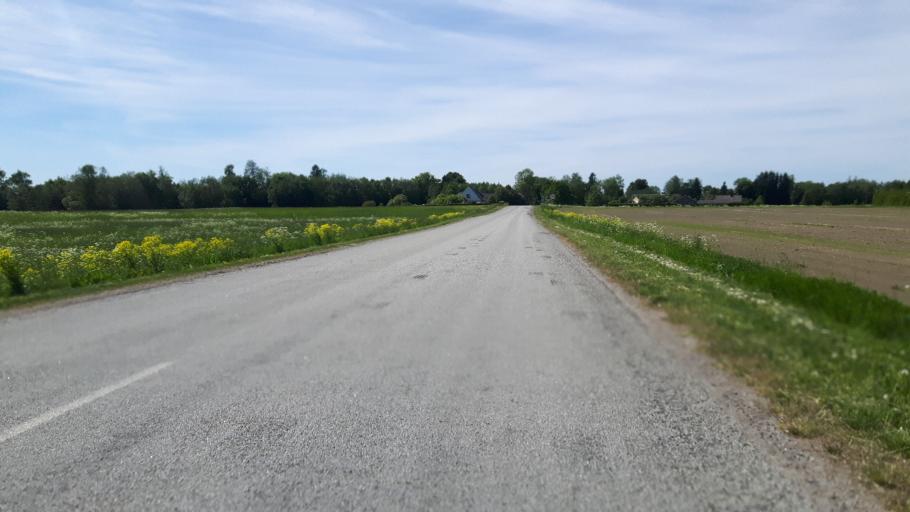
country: EE
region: Harju
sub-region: Kuusalu vald
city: Kuusalu
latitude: 59.4564
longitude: 25.3604
